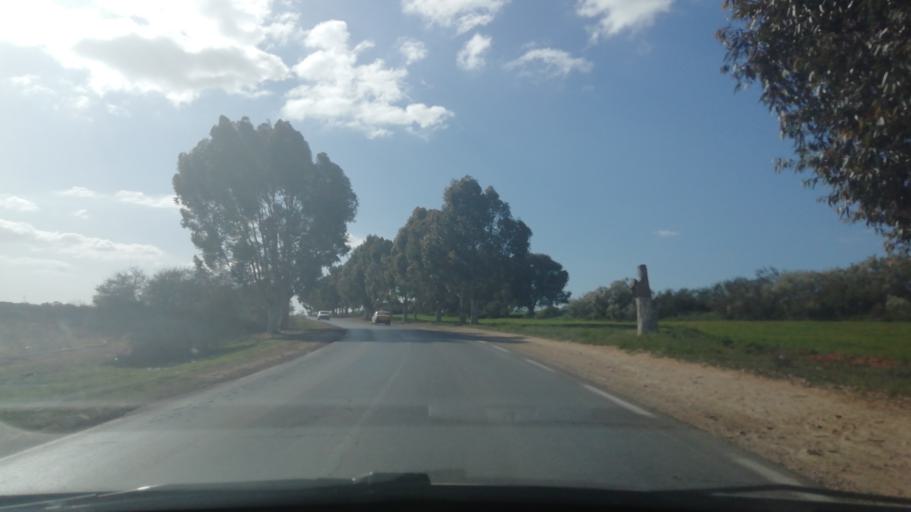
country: DZ
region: Mostaganem
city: Mostaganem
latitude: 35.9564
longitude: 0.2303
